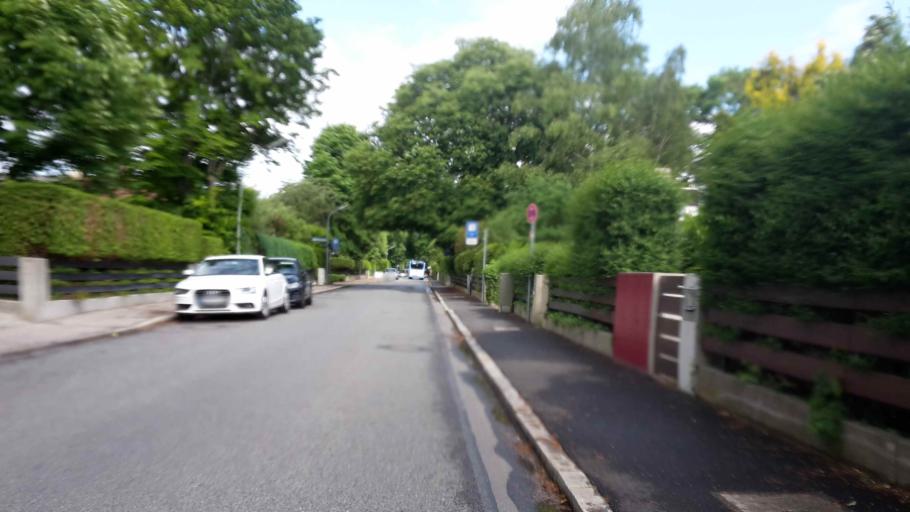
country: DE
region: Bavaria
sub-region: Upper Bavaria
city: Karlsfeld
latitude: 48.1991
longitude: 11.5194
